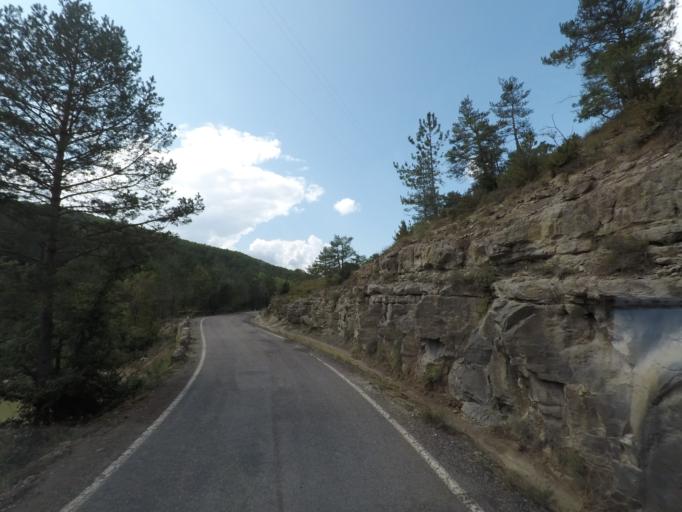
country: ES
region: Aragon
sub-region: Provincia de Huesca
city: Fiscal
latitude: 42.4080
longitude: -0.1945
